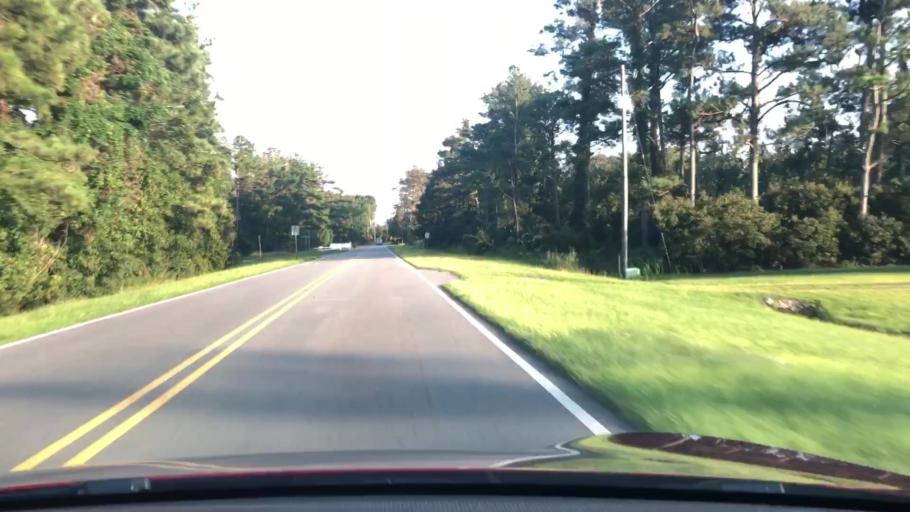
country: US
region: North Carolina
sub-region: Dare County
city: Manteo
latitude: 35.9018
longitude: -75.7720
